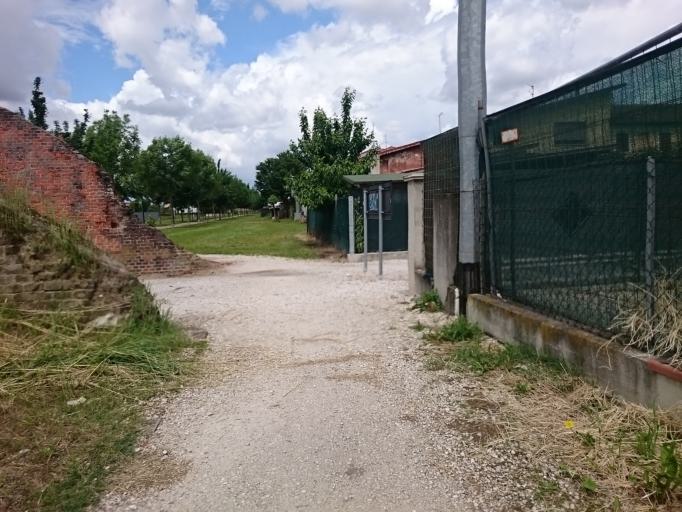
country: IT
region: Veneto
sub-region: Provincia di Padova
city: Piazzola sul Brenta
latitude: 45.5346
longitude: 11.7869
